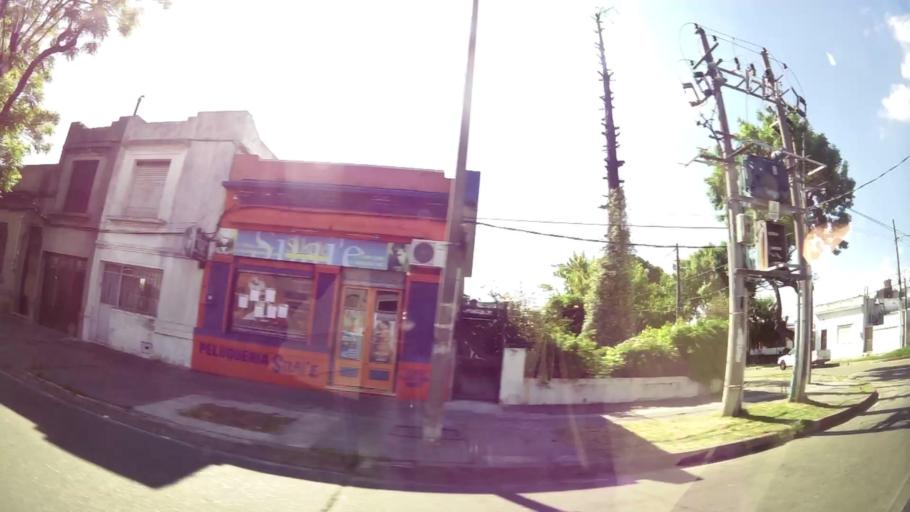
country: UY
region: Montevideo
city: Montevideo
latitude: -34.8469
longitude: -56.2127
